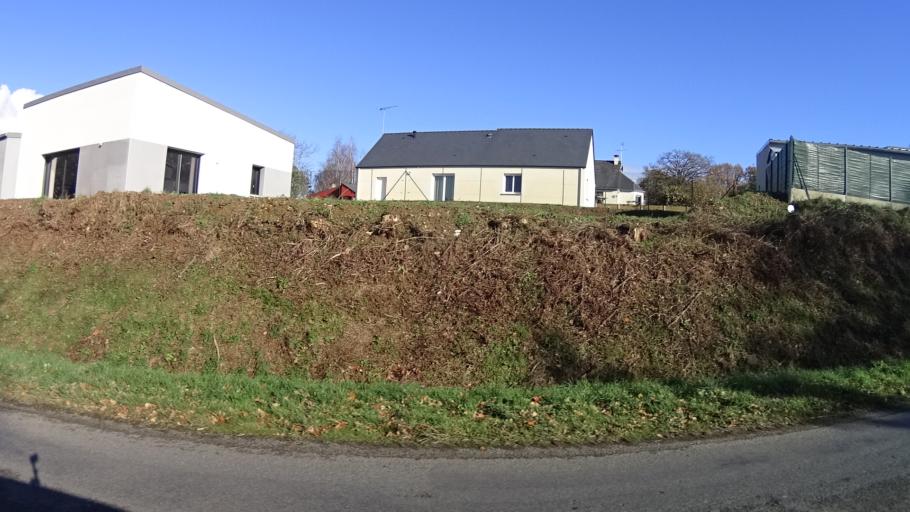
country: FR
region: Brittany
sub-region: Departement du Morbihan
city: Saint-Perreux
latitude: 47.6747
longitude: -2.0898
